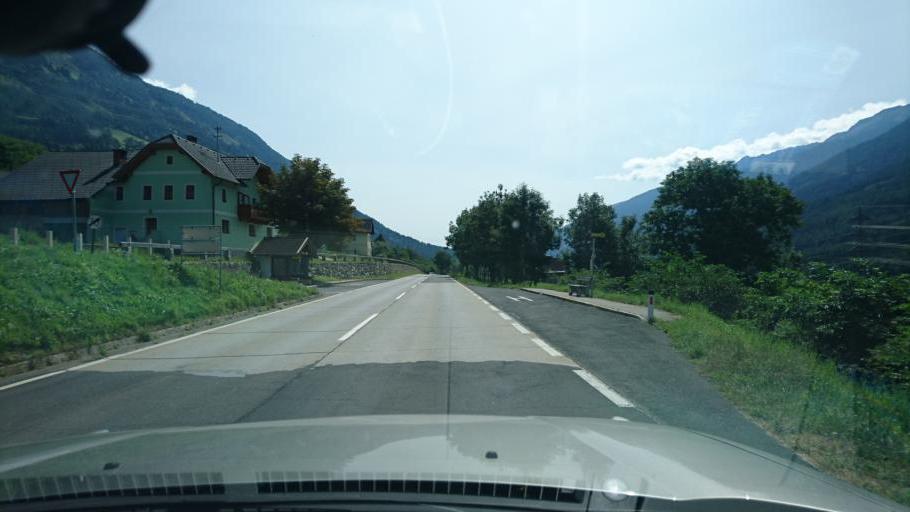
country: AT
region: Carinthia
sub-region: Politischer Bezirk Spittal an der Drau
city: Obervellach
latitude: 46.9163
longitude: 13.2377
